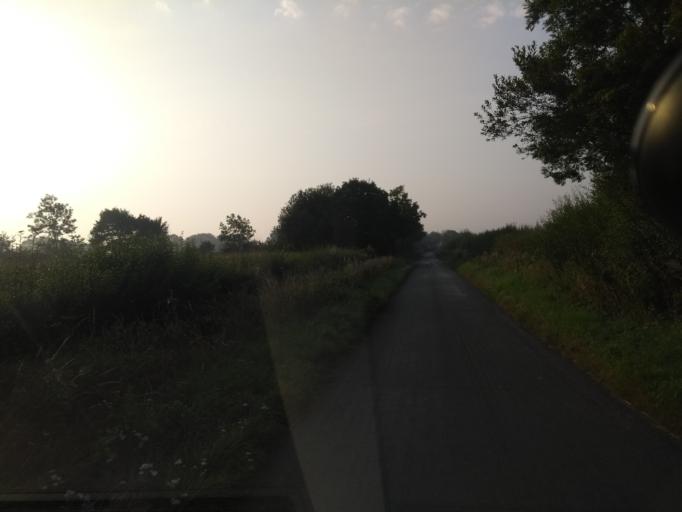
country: GB
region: England
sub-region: Somerset
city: Curry Rivel
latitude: 50.9911
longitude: -2.9142
